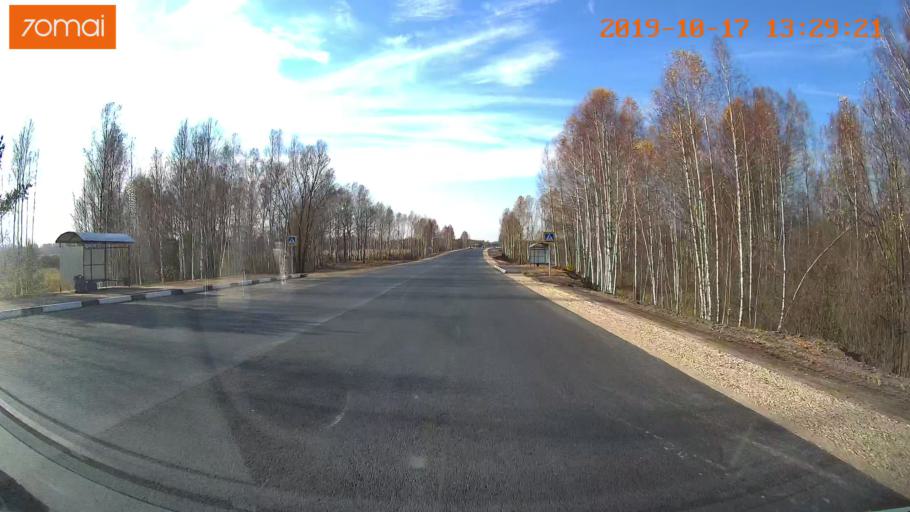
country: RU
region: Vladimir
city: Velikodvorskiy
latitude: 55.1191
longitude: 40.8436
